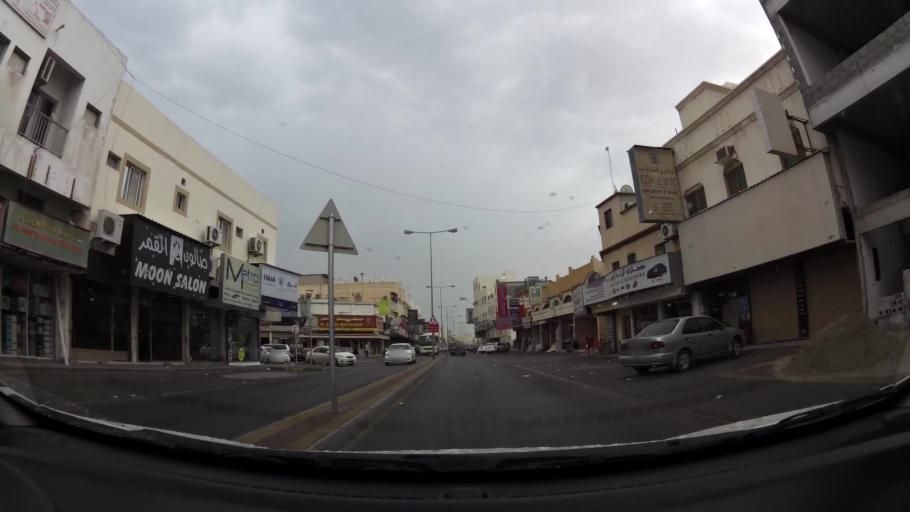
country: BH
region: Northern
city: Madinat `Isa
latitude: 26.1711
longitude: 50.5632
